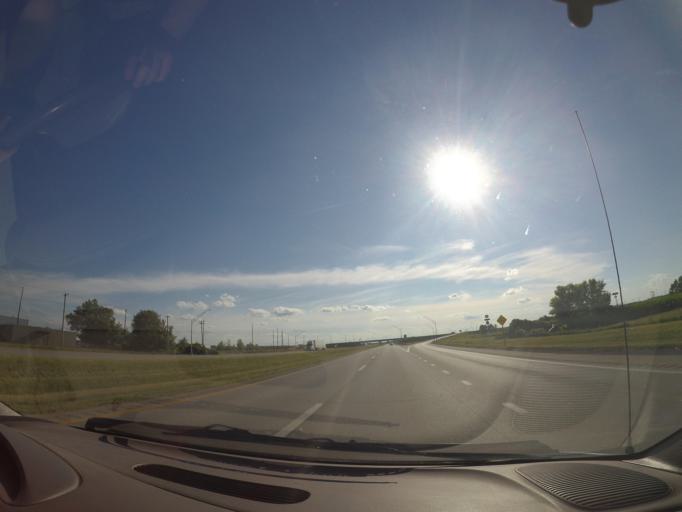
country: US
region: Ohio
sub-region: Henry County
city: Napoleon
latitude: 41.4152
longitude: -84.0991
